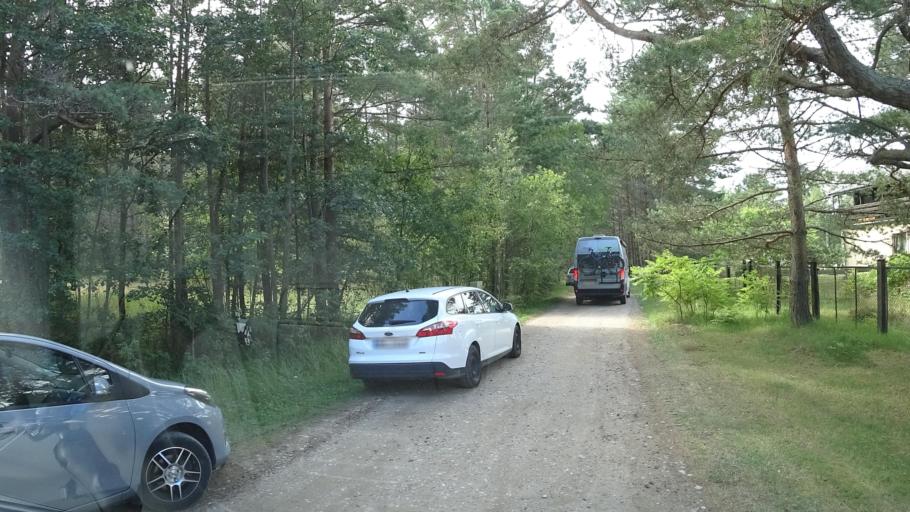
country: LV
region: Ventspils
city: Ventspils
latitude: 57.4893
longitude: 21.6489
